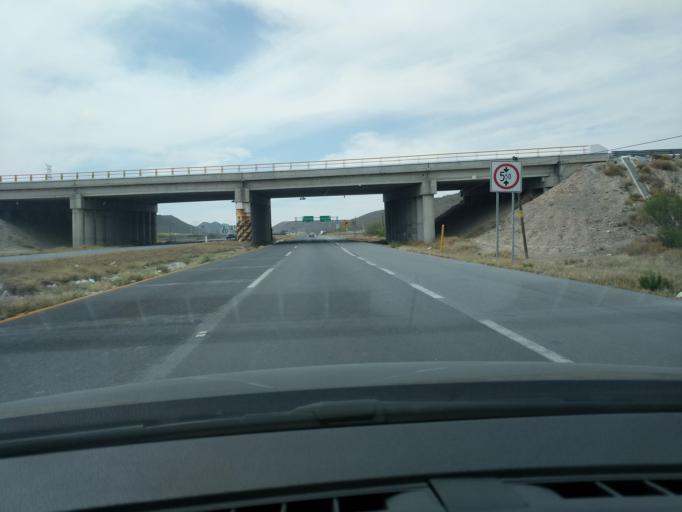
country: MX
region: Coahuila
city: Saltillo
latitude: 25.4536
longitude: -101.0650
